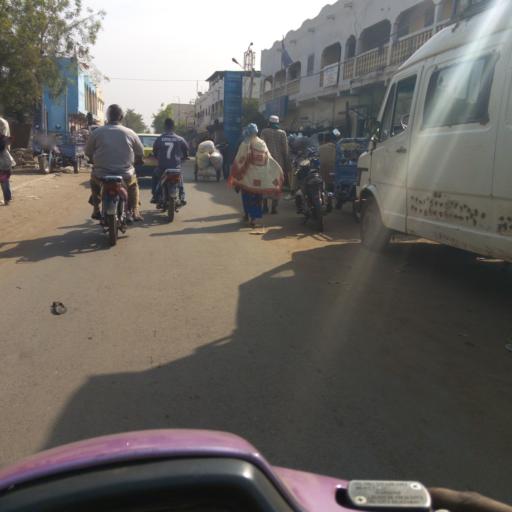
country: ML
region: Bamako
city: Bamako
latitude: 12.6463
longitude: -7.9914
